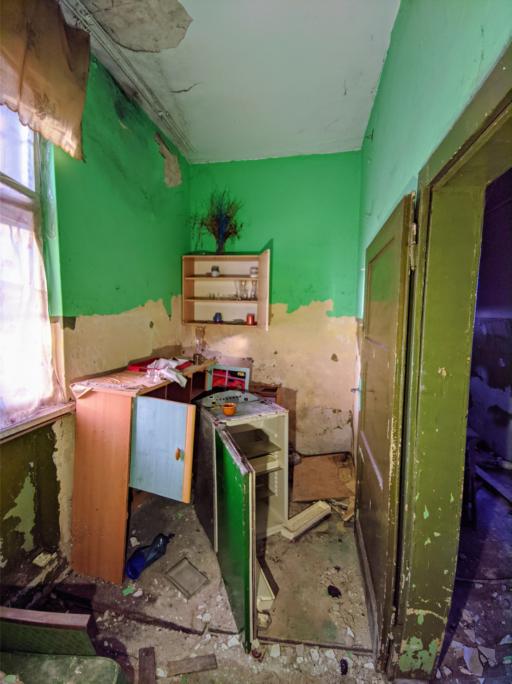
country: PL
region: Lubusz
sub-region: Powiat zaganski
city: Zagan
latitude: 51.6042
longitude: 15.3132
